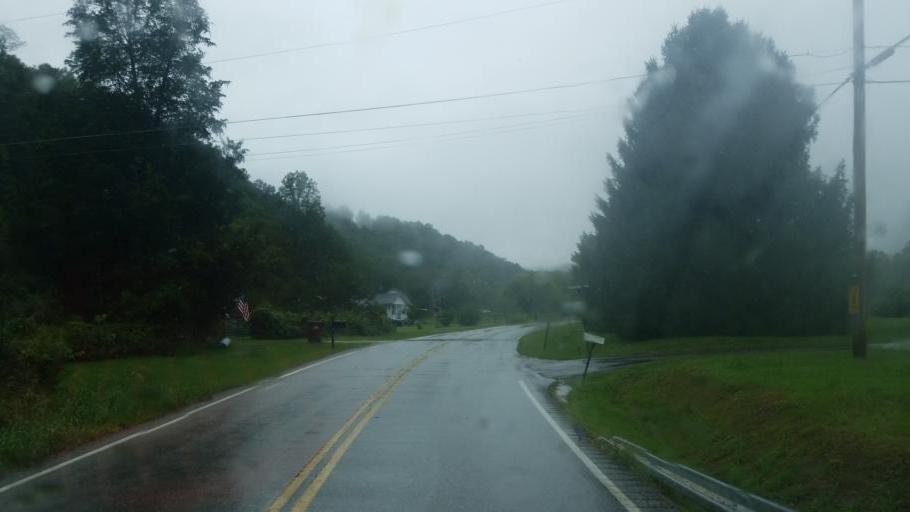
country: US
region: Kentucky
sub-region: Greenup County
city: South Shore
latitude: 38.6652
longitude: -82.9190
